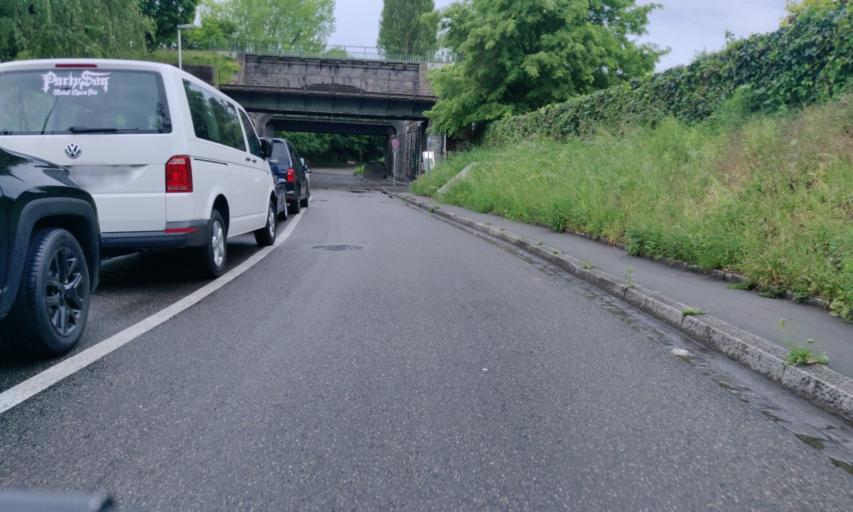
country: CH
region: Basel-Landschaft
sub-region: Bezirk Arlesheim
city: Birsfelden
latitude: 47.5660
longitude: 7.6295
